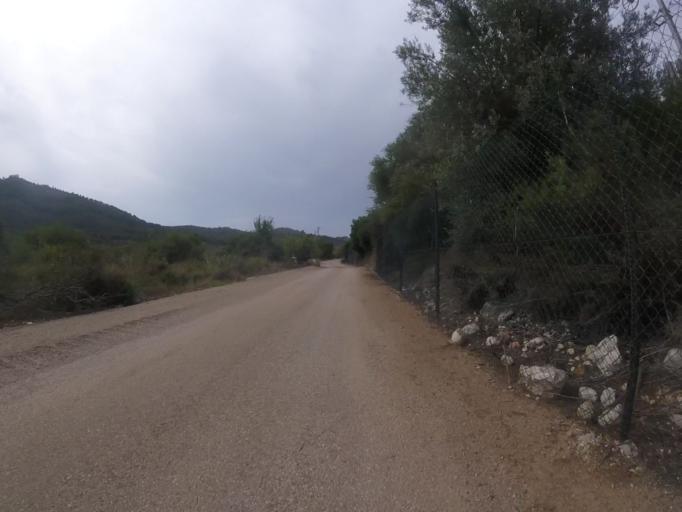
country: ES
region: Valencia
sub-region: Provincia de Castello
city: Alcoceber
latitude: 40.2644
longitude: 0.2548
